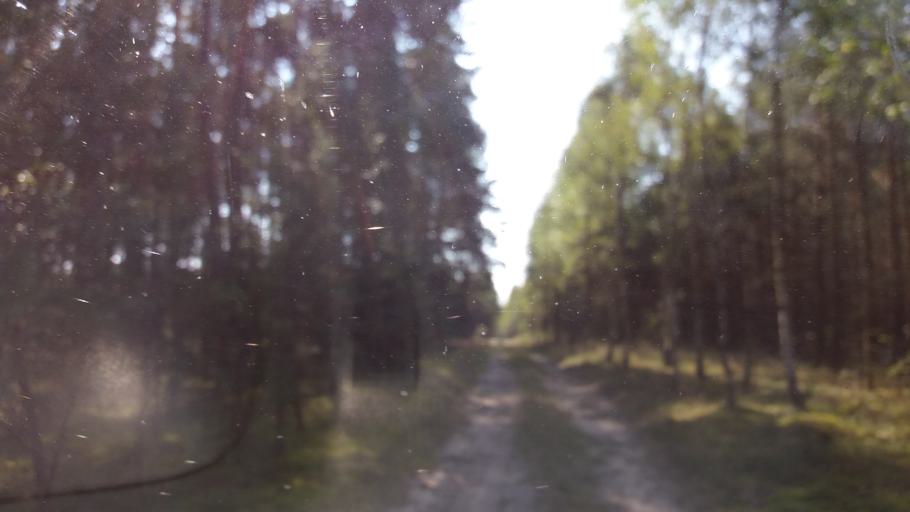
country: PL
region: West Pomeranian Voivodeship
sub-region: Powiat walecki
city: Tuczno
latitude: 53.2080
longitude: 16.0178
